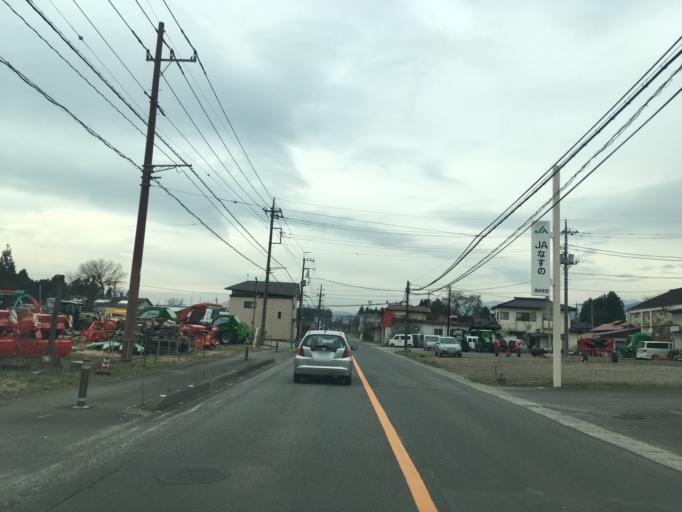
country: JP
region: Tochigi
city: Kuroiso
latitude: 36.9901
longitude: 139.9388
